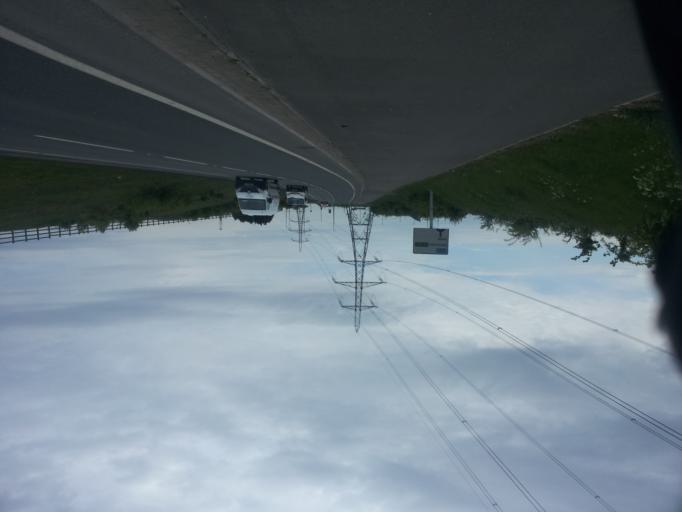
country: GB
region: England
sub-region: Kent
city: Sittingbourne
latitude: 51.3600
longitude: 0.7502
